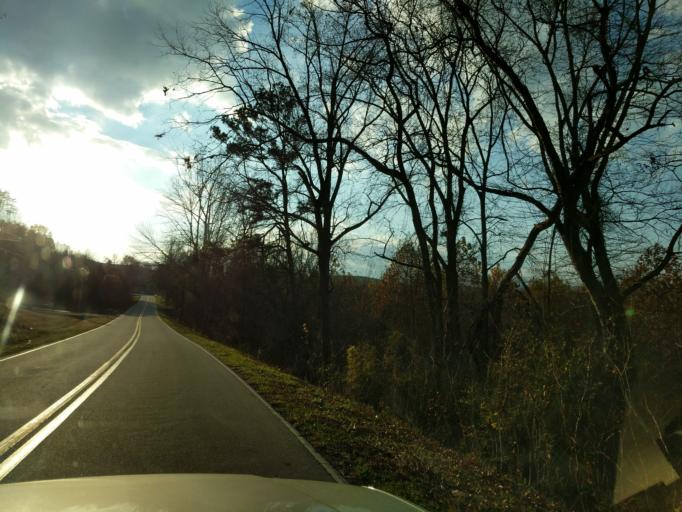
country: US
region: North Carolina
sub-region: Rutherford County
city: Rutherfordton
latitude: 35.2941
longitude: -81.9847
